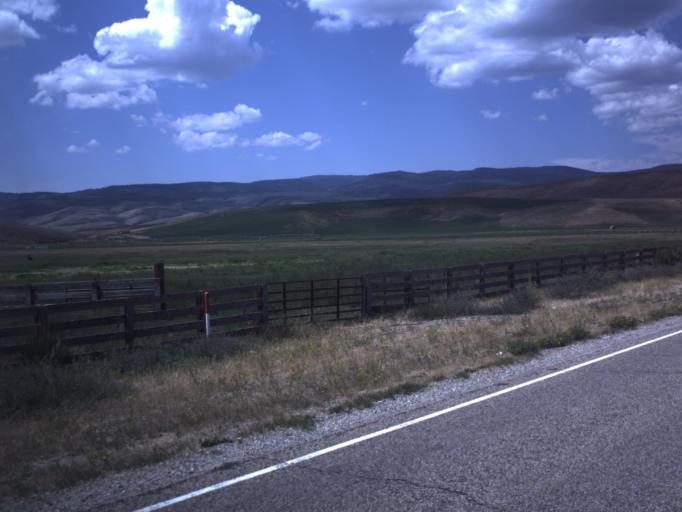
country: US
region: Utah
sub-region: Rich County
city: Randolph
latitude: 41.8423
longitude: -111.3463
